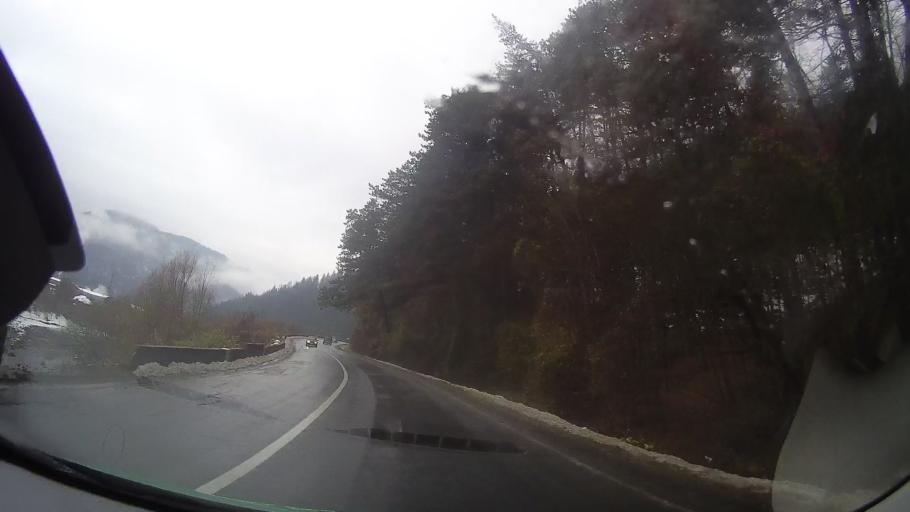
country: RO
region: Neamt
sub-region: Comuna Tarcau
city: Tarcau
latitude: 46.8928
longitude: 26.1379
